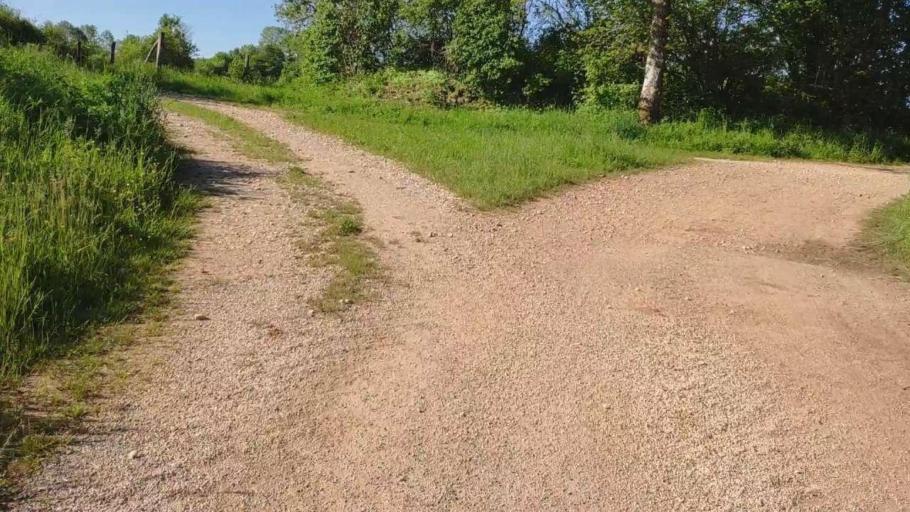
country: FR
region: Franche-Comte
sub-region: Departement du Jura
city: Perrigny
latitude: 46.6806
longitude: 5.6520
